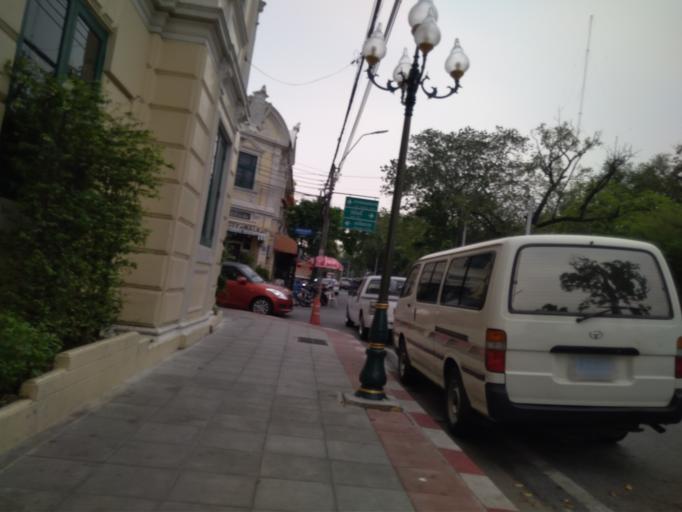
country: TH
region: Bangkok
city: Bangkok
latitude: 13.7484
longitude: 100.4965
